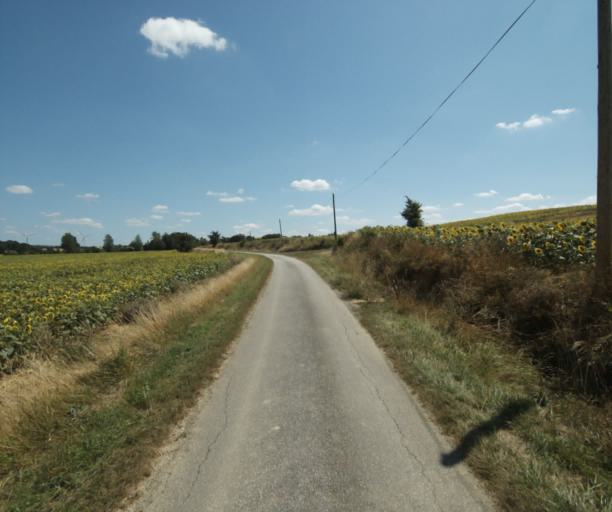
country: FR
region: Midi-Pyrenees
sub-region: Departement de la Haute-Garonne
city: Saint-Felix-Lauragais
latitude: 43.4690
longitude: 1.8858
